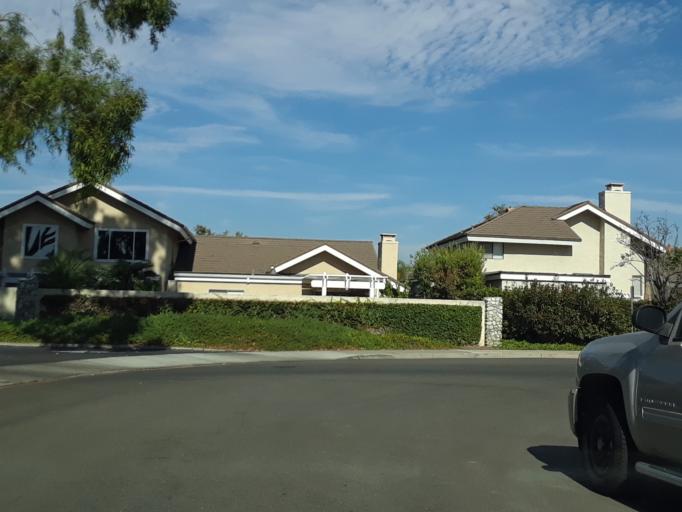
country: US
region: California
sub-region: Orange County
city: Irvine
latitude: 33.6803
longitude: -117.7936
